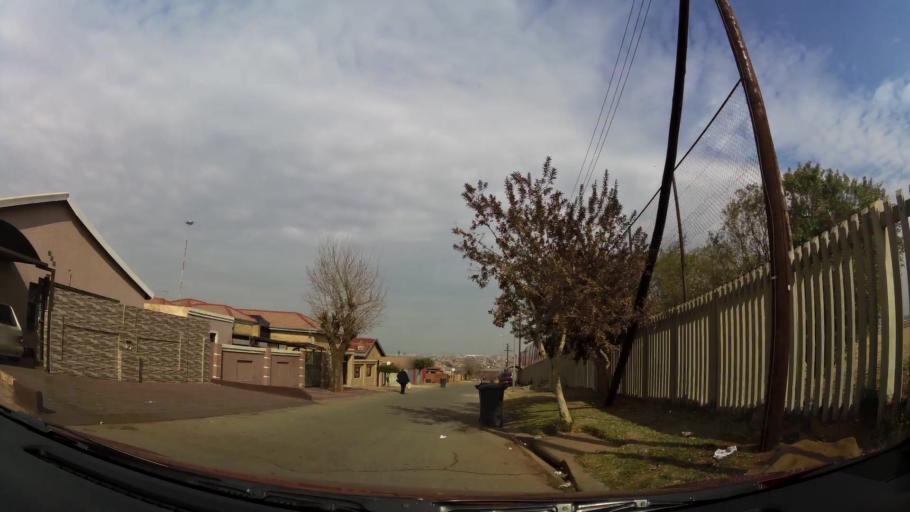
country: ZA
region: Gauteng
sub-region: City of Johannesburg Metropolitan Municipality
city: Soweto
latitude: -26.2610
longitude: 27.8209
